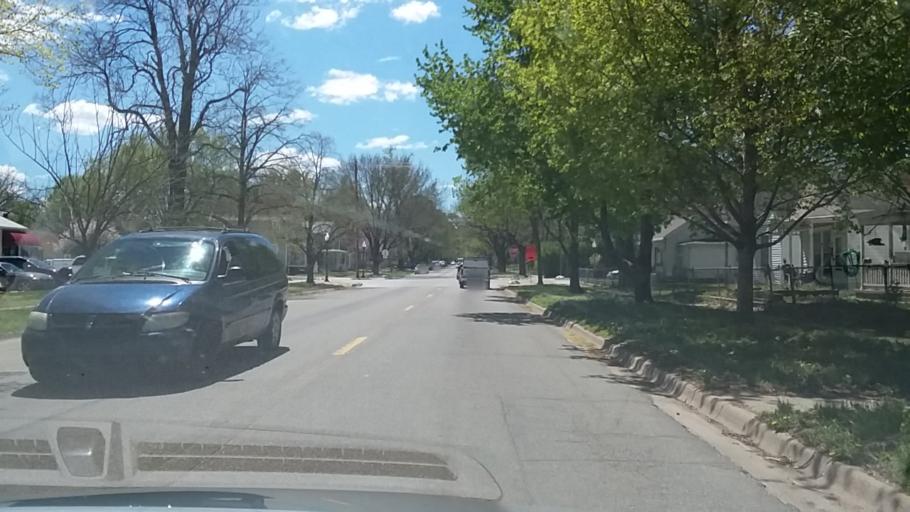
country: US
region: Kansas
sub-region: Douglas County
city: Lawrence
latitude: 38.9682
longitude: -95.2325
